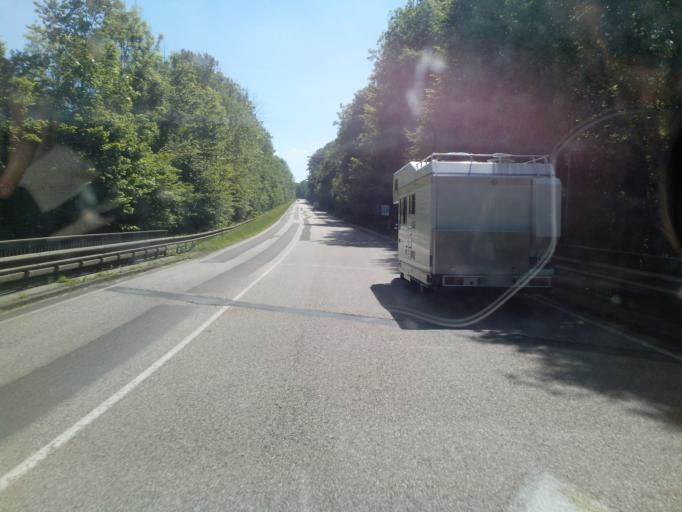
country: FR
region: Haute-Normandie
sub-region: Departement de l'Eure
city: Toutainville
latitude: 49.3897
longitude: 0.4089
